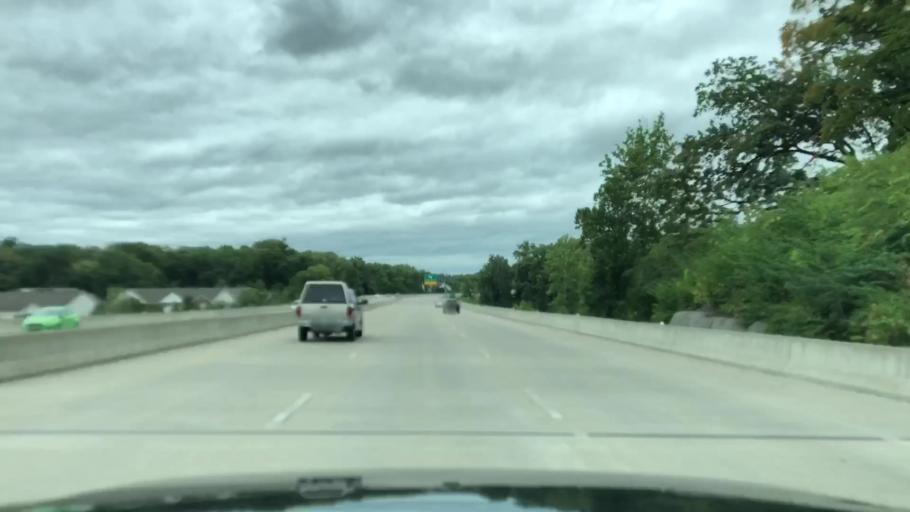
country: US
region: Missouri
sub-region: Saint Louis County
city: Maryland Heights
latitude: 38.6920
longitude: -90.4989
